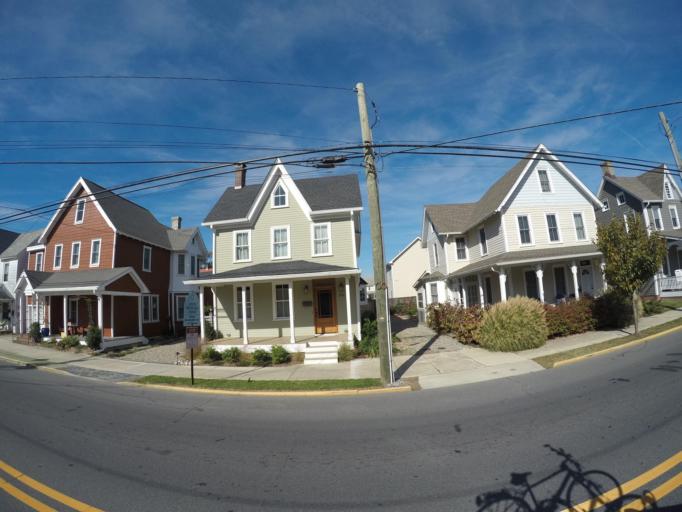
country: US
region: Delaware
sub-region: Sussex County
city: Lewes
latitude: 38.7720
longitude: -75.1416
